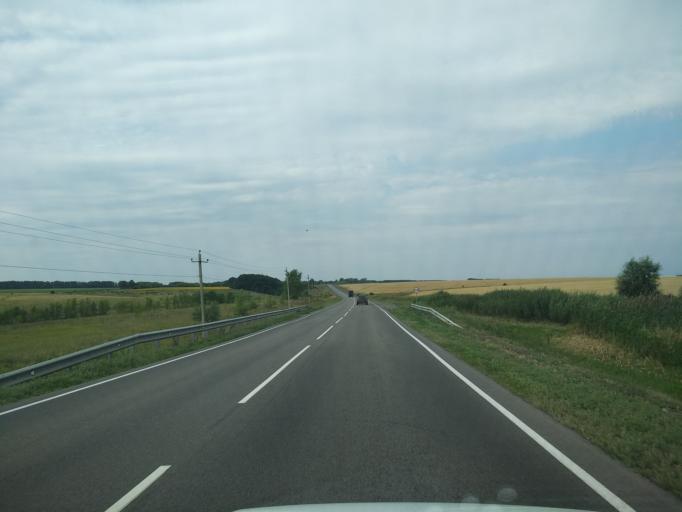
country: RU
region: Voronezj
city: Pereleshinskiy
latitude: 51.8216
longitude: 40.2705
